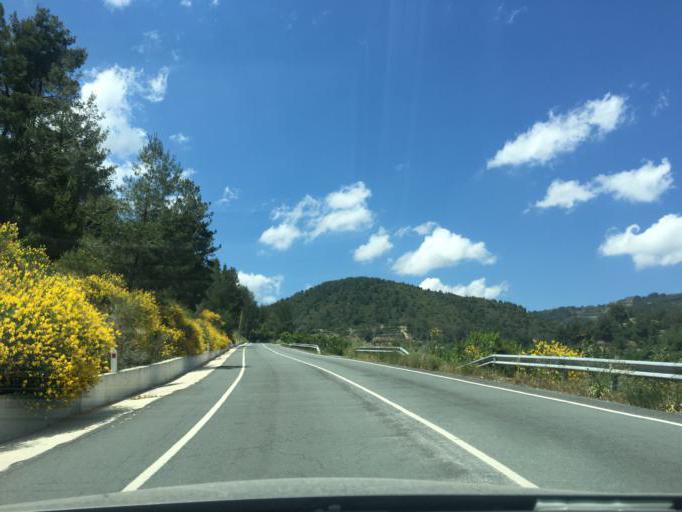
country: CY
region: Limassol
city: Pelendri
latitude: 34.9095
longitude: 32.9431
